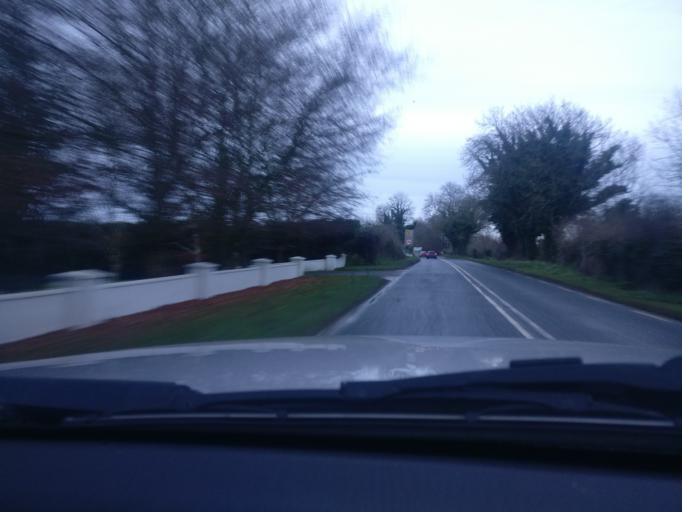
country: IE
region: Leinster
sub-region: An Mhi
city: Kells
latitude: 53.7188
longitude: -6.8414
